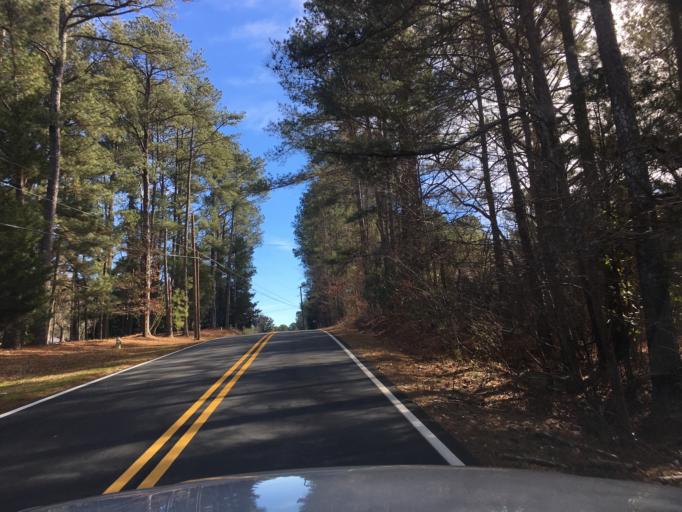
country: US
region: Georgia
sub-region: Rockdale County
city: Lakeview Estates
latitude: 33.7377
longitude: -84.0341
